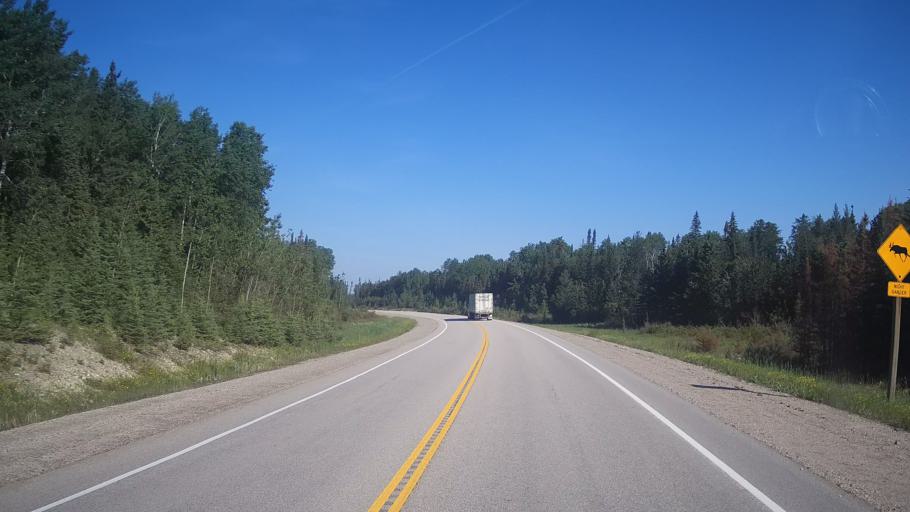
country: CA
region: Ontario
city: Dryden
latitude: 49.5856
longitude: -92.2654
